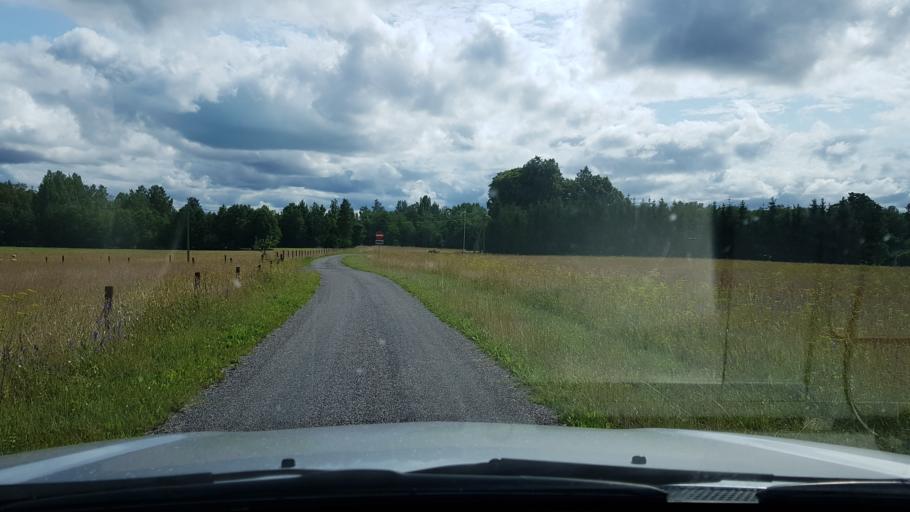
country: EE
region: Ida-Virumaa
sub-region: Narva-Joesuu linn
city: Narva-Joesuu
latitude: 59.3687
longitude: 27.9534
